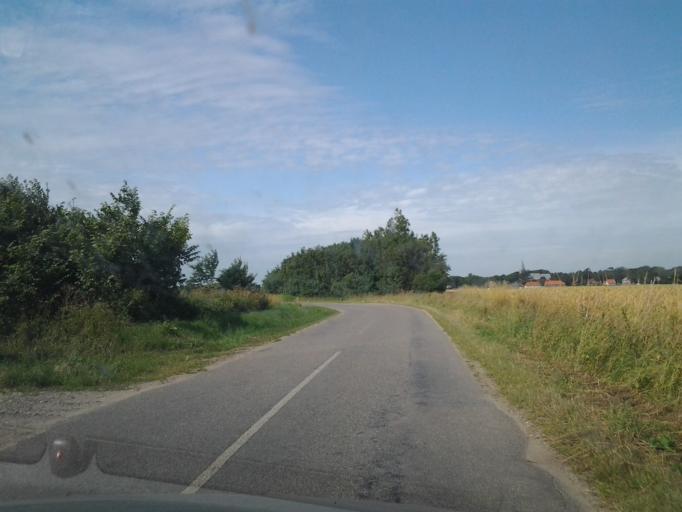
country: DE
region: Schleswig-Holstein
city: Aventoft
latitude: 54.9308
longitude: 8.7987
